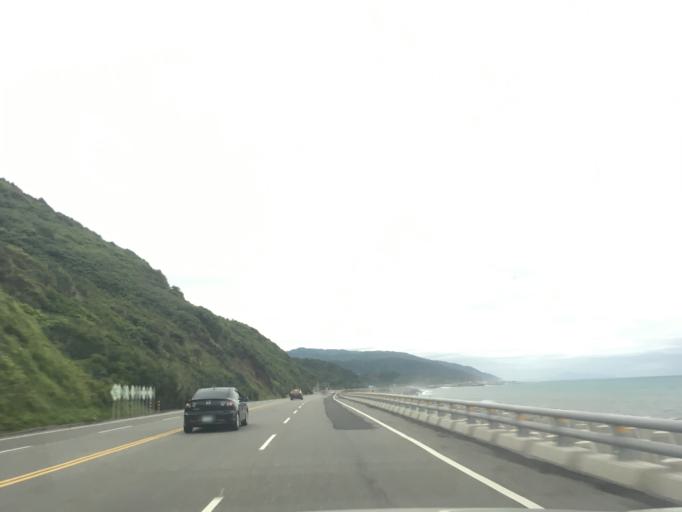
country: TW
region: Taiwan
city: Hengchun
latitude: 22.3179
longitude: 120.8916
